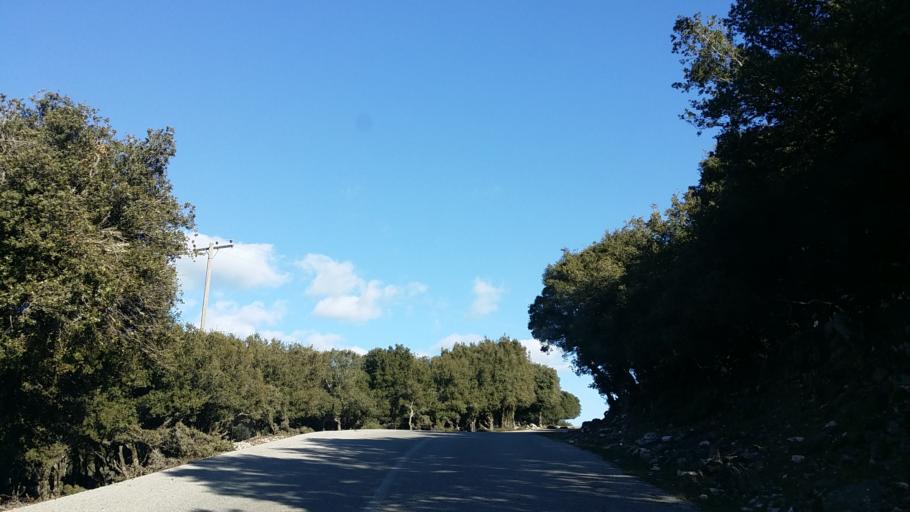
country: GR
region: Central Greece
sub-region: Nomos Evrytanias
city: Kerasochori
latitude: 38.9677
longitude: 21.5961
